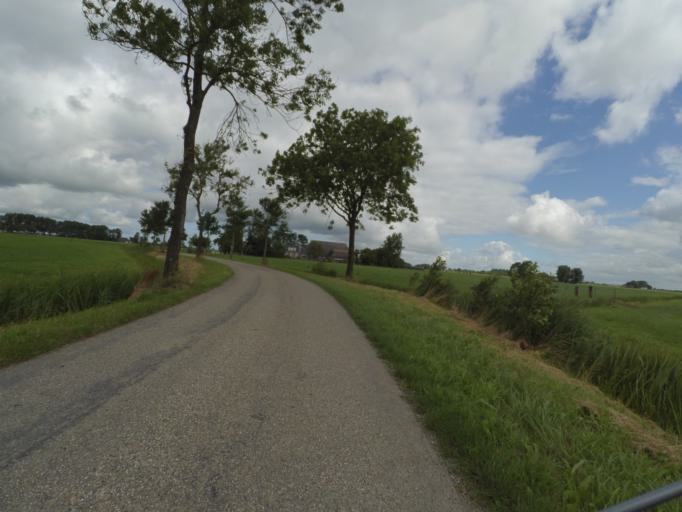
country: NL
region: Friesland
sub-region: Gemeente Kollumerland en Nieuwkruisland
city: Kollum
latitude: 53.2852
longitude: 6.2257
